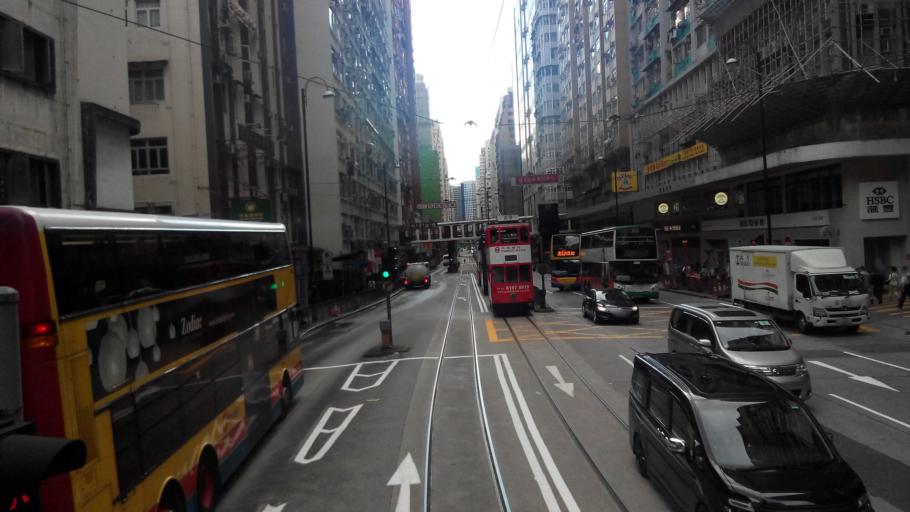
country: HK
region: Wanchai
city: Wan Chai
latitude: 22.2901
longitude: 114.1956
